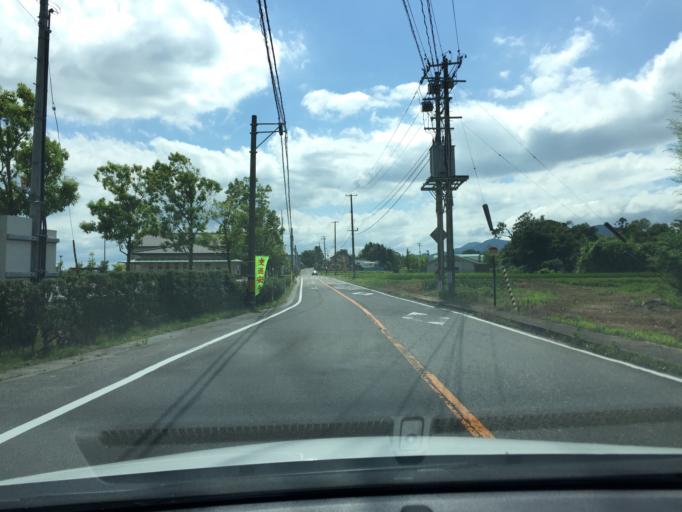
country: JP
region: Fukushima
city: Koriyama
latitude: 37.3576
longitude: 140.2883
